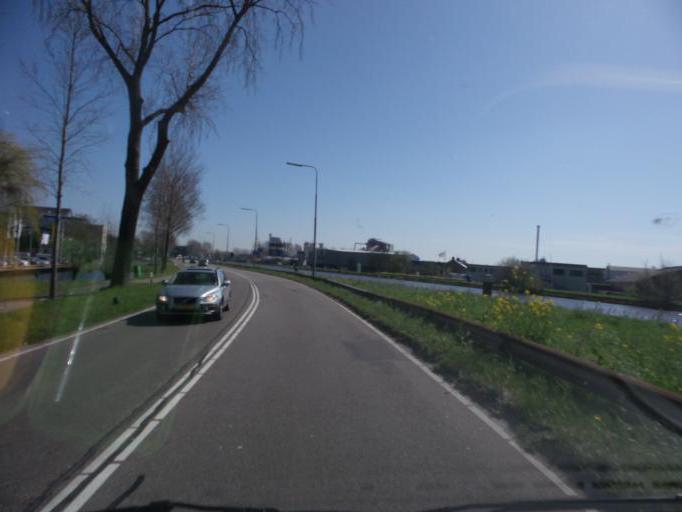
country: NL
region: South Holland
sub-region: Gemeente Gouda
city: Bloemendaal
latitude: 52.0150
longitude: 4.6864
